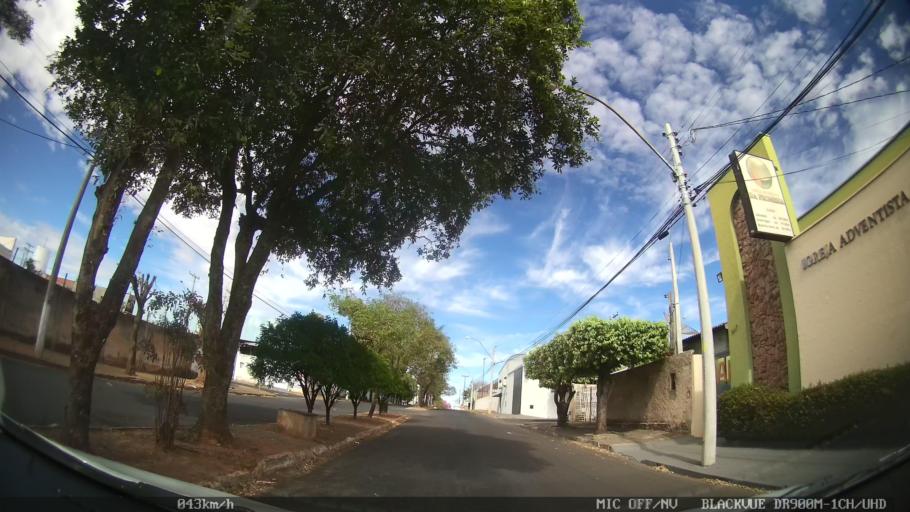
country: BR
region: Sao Paulo
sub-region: Bady Bassitt
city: Bady Bassitt
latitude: -20.8181
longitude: -49.5233
